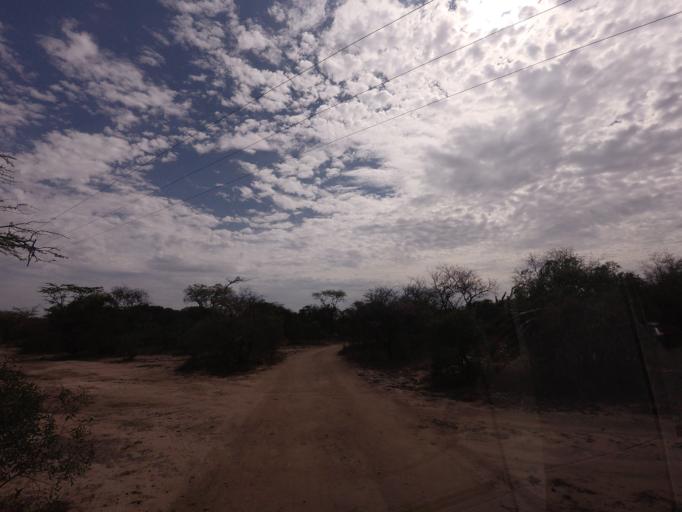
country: ZA
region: Limpopo
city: Thulamahashi
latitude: -24.5269
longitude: 31.1142
